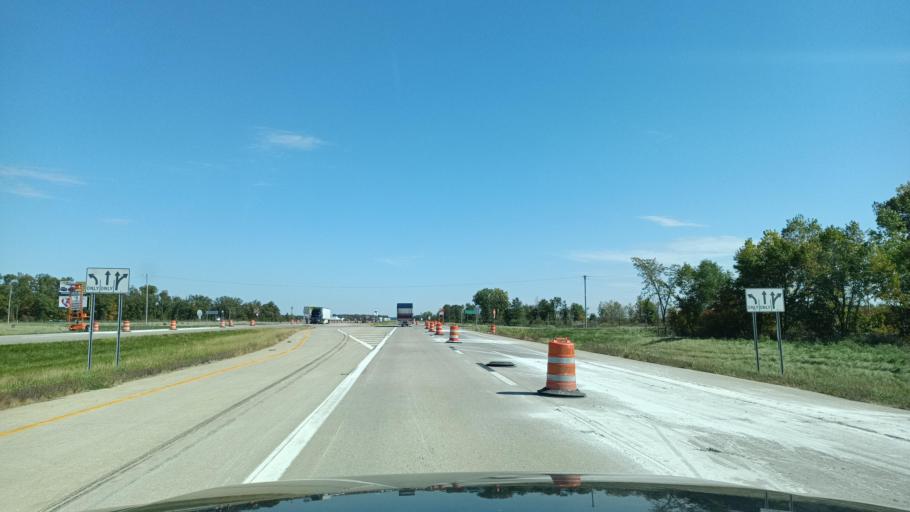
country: US
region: Ohio
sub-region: Defiance County
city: Defiance
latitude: 41.2509
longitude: -84.4781
